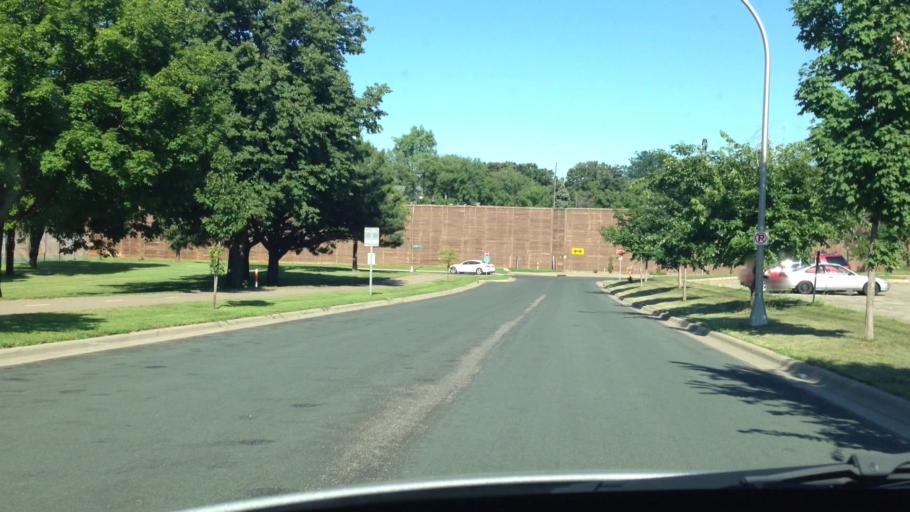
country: US
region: Minnesota
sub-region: Hennepin County
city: Richfield
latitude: 44.8673
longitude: -93.3008
